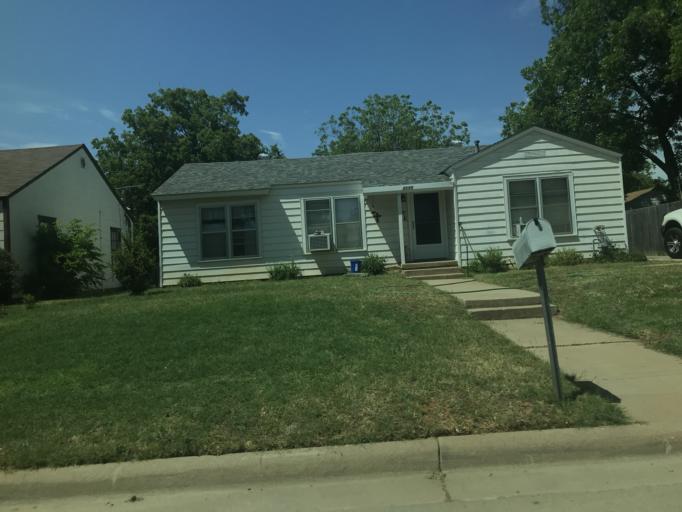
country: US
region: Texas
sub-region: Taylor County
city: Abilene
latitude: 32.4358
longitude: -99.7601
